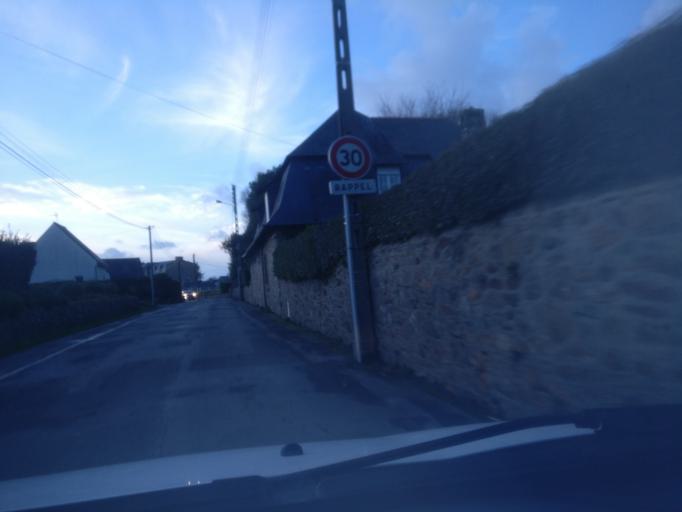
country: FR
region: Brittany
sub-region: Departement des Cotes-d'Armor
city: Perros-Guirec
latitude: 48.8190
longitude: -3.4674
